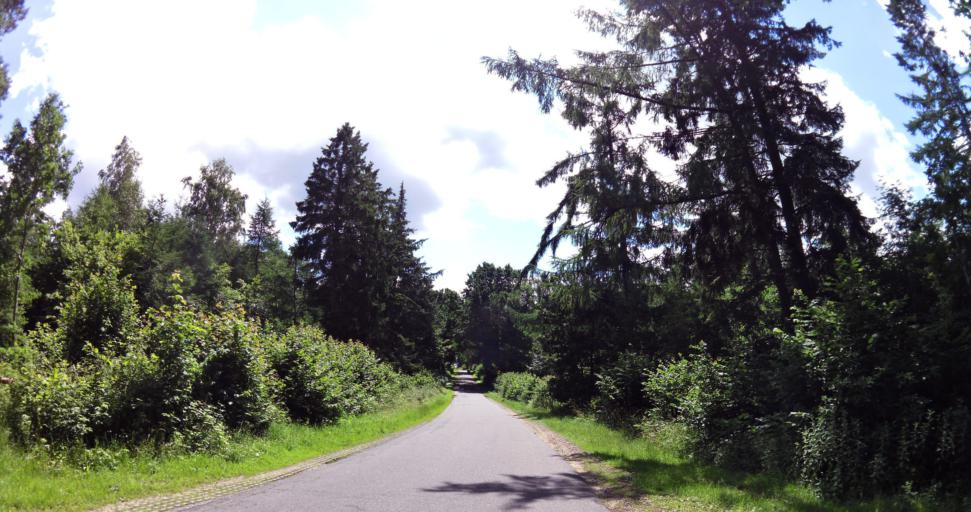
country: DE
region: Schleswig-Holstein
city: Brodersby
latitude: 54.5106
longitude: 9.7196
